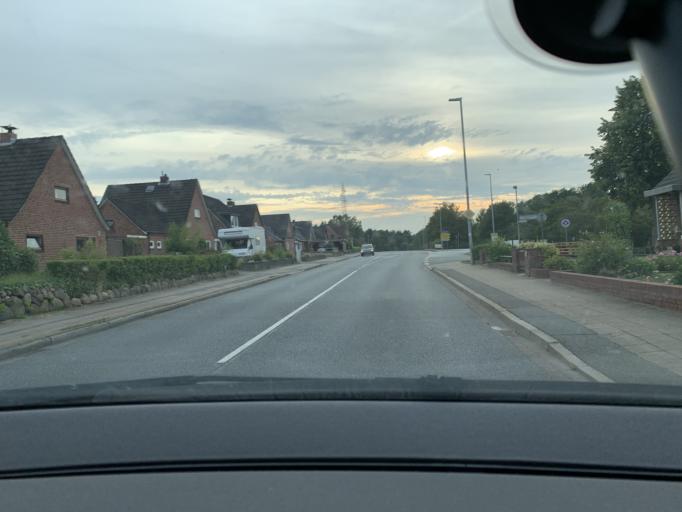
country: DE
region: Schleswig-Holstein
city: Mildstedt
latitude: 54.4717
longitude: 9.0837
